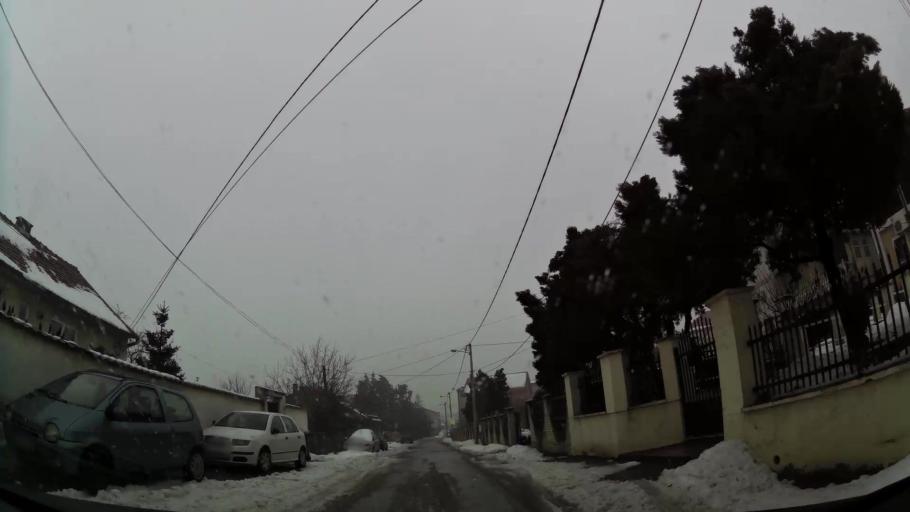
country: RS
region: Central Serbia
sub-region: Belgrade
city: Zvezdara
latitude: 44.7735
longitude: 20.5336
